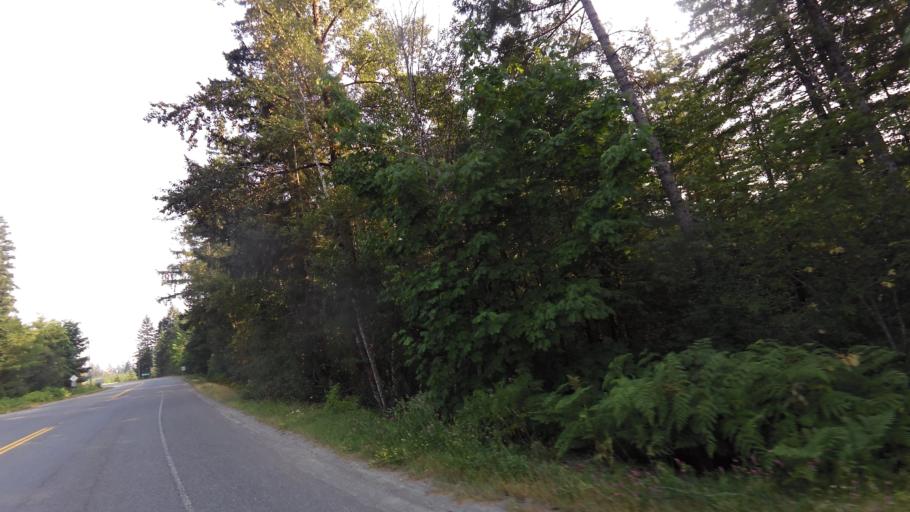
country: CA
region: British Columbia
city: Port Alberni
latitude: 49.2958
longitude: -124.9258
